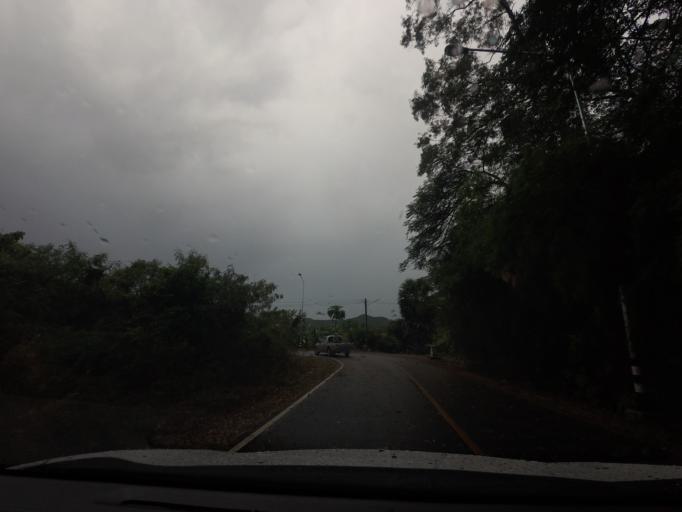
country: TH
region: Rayong
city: Ban Chang
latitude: 12.7596
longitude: 100.9575
